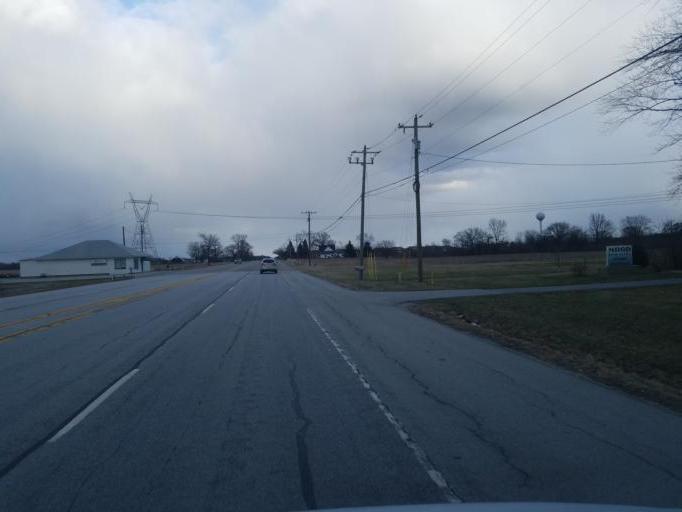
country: US
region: Indiana
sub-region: Hancock County
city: New Palestine
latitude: 39.7795
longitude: -85.8933
